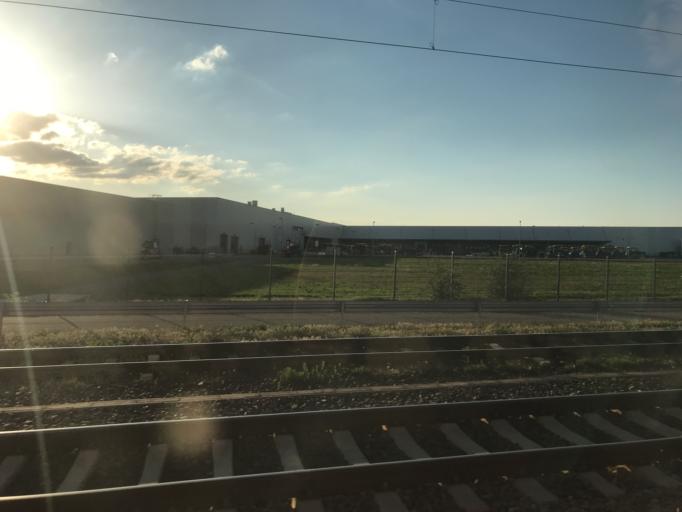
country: DE
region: Rheinland-Pfalz
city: Limburgerhof
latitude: 49.4394
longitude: 8.4030
